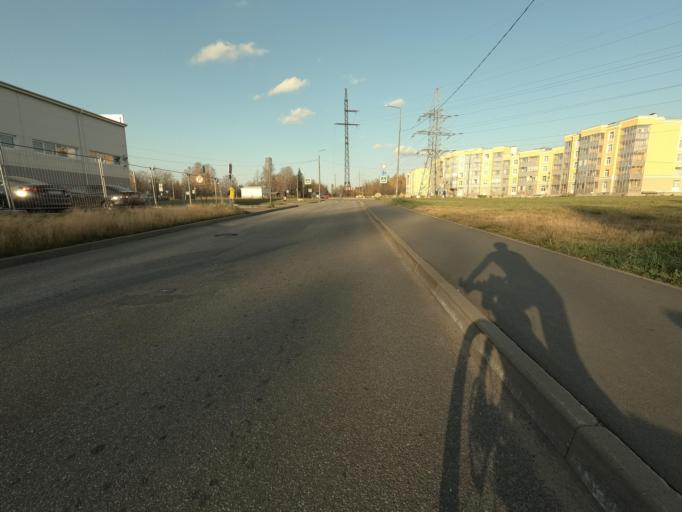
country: RU
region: Leningrad
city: Sertolovo
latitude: 60.1653
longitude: 30.1860
